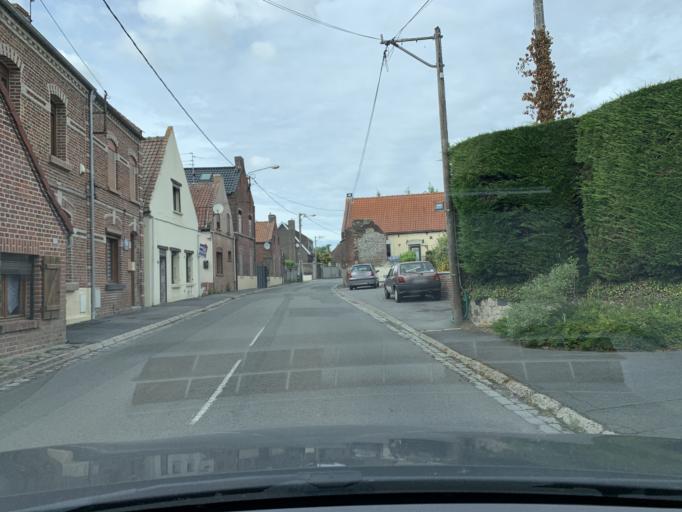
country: FR
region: Nord-Pas-de-Calais
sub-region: Departement du Nord
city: Lewarde
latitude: 50.3389
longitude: 3.1628
